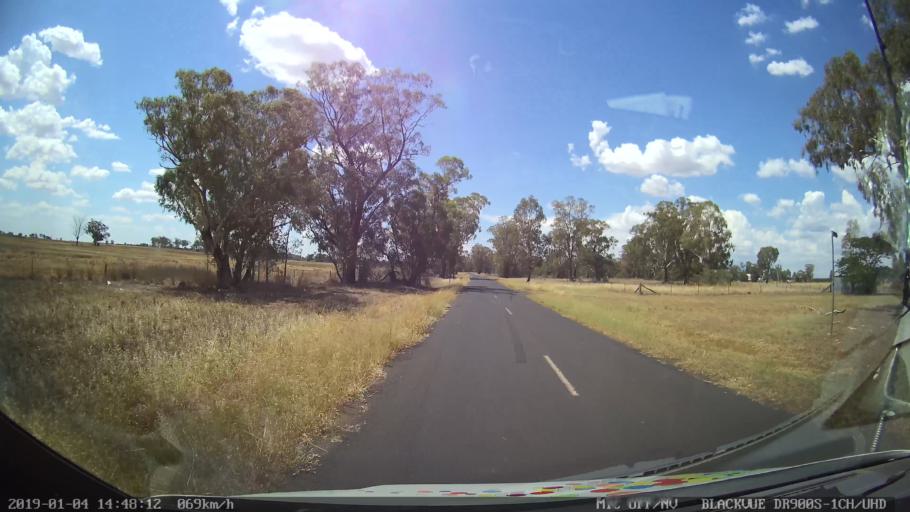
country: AU
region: New South Wales
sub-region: Dubbo Municipality
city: Dubbo
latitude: -32.0616
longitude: 148.6629
